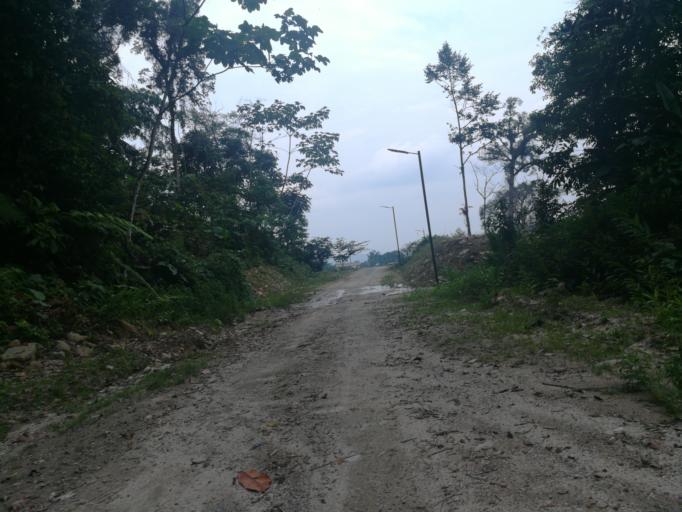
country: EC
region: Napo
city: Archidona
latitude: -0.9457
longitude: -77.8936
